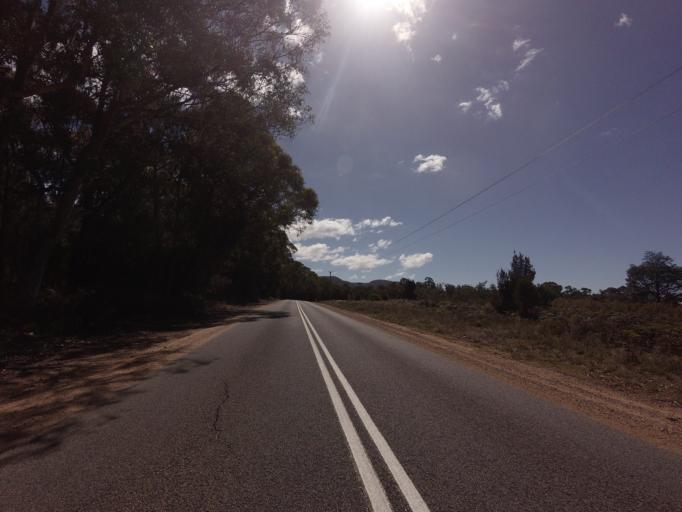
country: AU
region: Tasmania
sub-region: Break O'Day
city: St Helens
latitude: -41.6773
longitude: 148.2783
